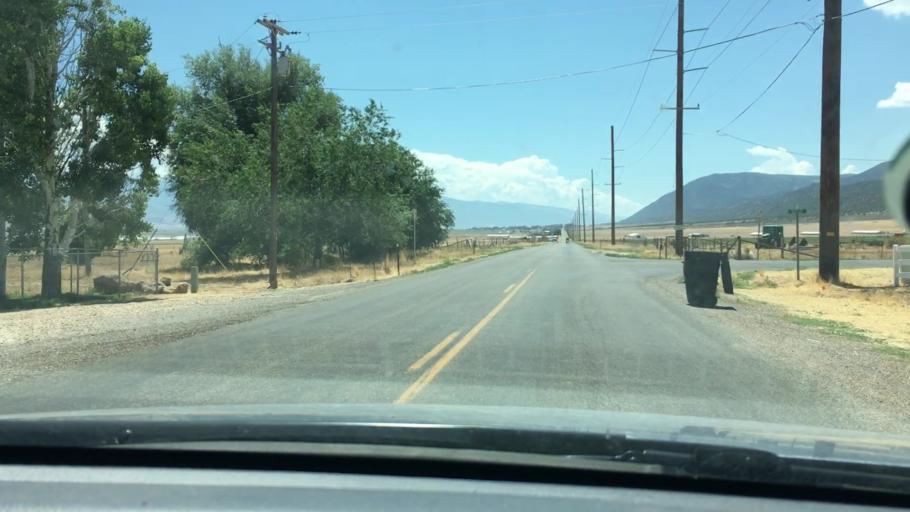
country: US
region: Utah
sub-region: Sanpete County
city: Moroni
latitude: 39.5424
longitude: -111.6400
